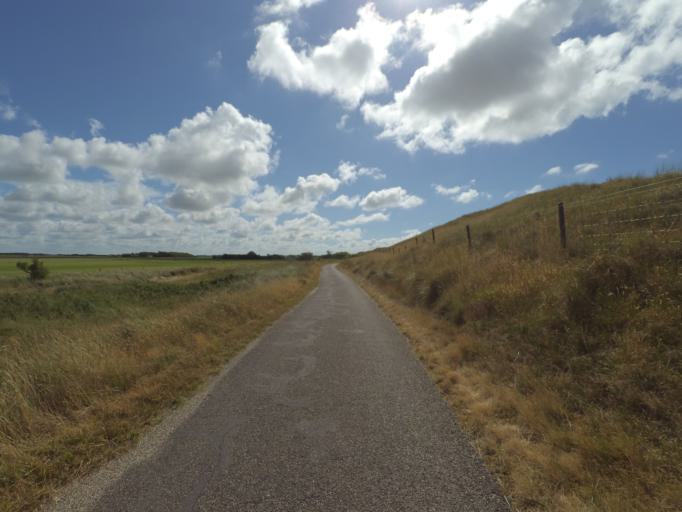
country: NL
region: North Holland
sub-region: Gemeente Texel
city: Den Burg
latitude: 53.1376
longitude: 4.8244
